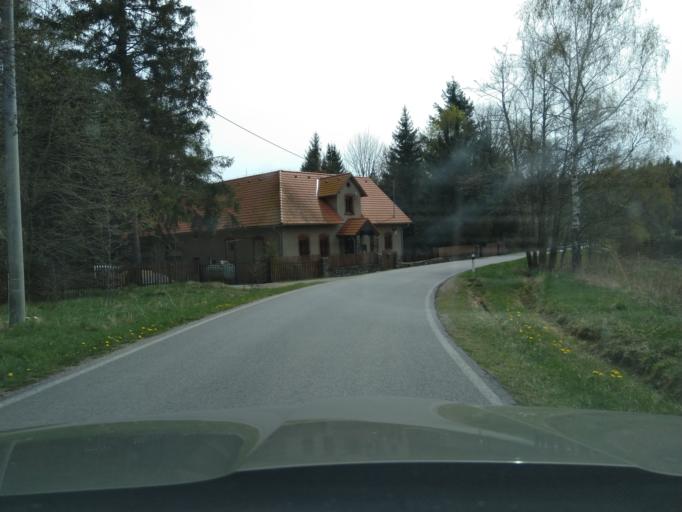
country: CZ
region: Jihocesky
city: Vacov
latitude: 49.1628
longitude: 13.6874
